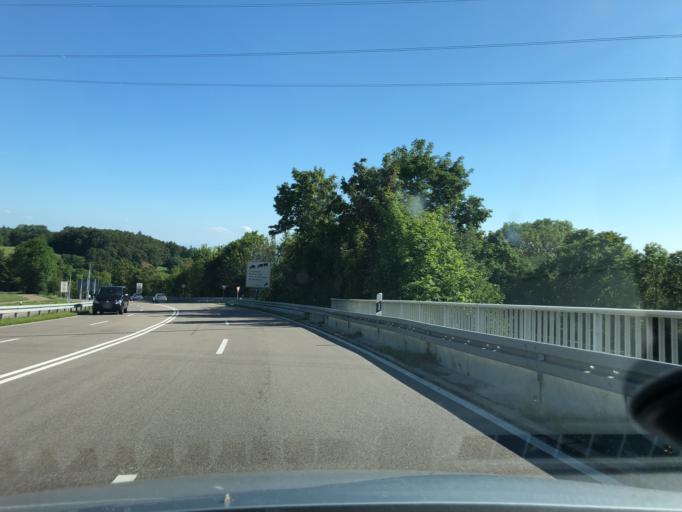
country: DE
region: Baden-Wuerttemberg
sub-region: Freiburg Region
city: Dogern
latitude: 47.6511
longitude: 8.1752
